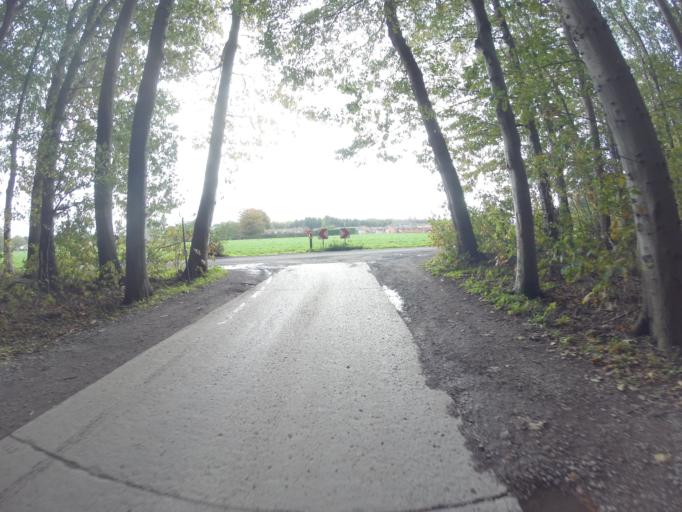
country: BE
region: Flanders
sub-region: Provincie West-Vlaanderen
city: Ruiselede
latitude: 51.0854
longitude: 3.3675
